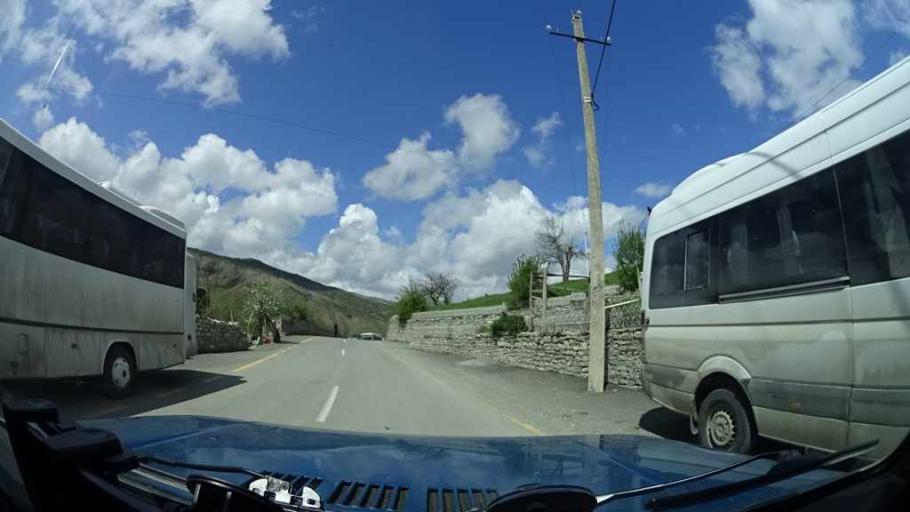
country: AZ
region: Ismayilli
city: Basqal
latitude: 40.8433
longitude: 48.3769
